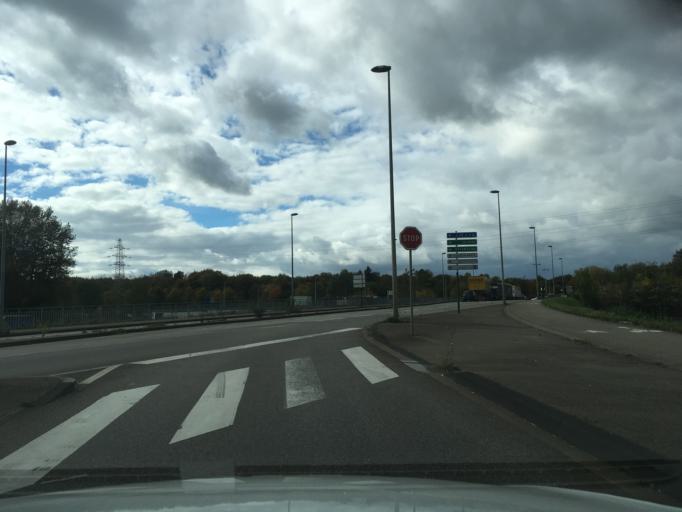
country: DE
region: Baden-Wuerttemberg
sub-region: Freiburg Region
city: Kehl
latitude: 48.5247
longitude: 7.7811
